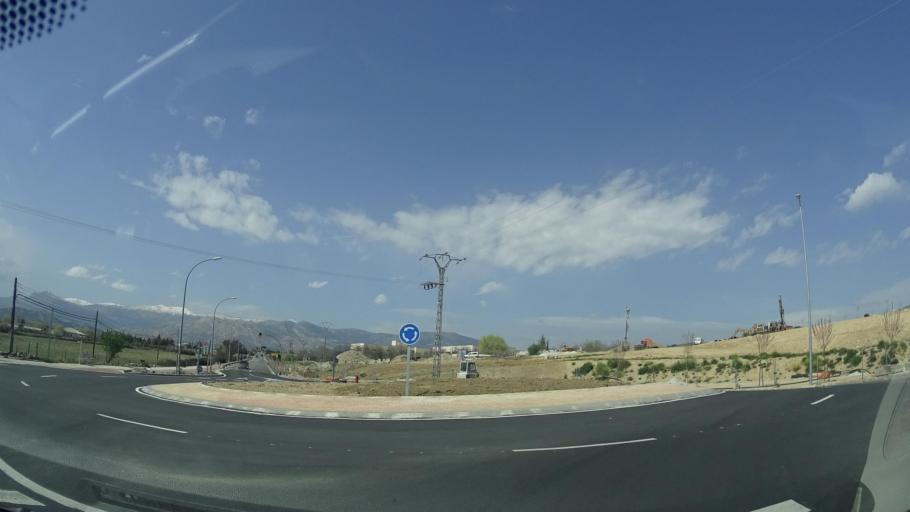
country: ES
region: Madrid
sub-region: Provincia de Madrid
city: Colmenar Viejo
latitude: 40.6761
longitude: -3.7795
